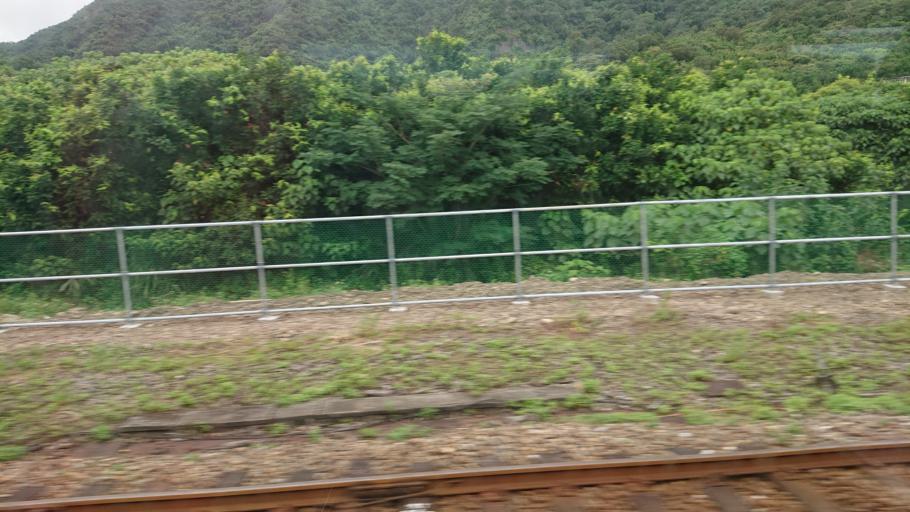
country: TW
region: Taiwan
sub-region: Keelung
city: Keelung
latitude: 24.9641
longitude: 121.9210
